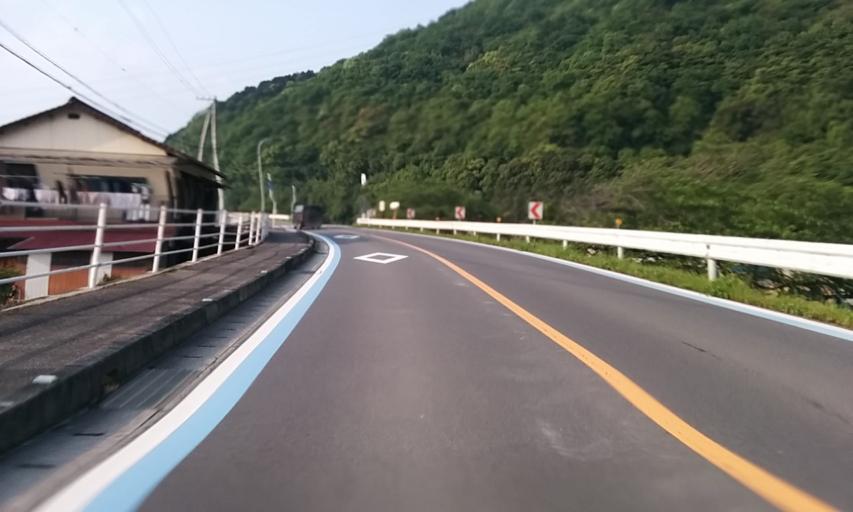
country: JP
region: Ehime
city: Saijo
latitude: 33.8935
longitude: 133.1944
